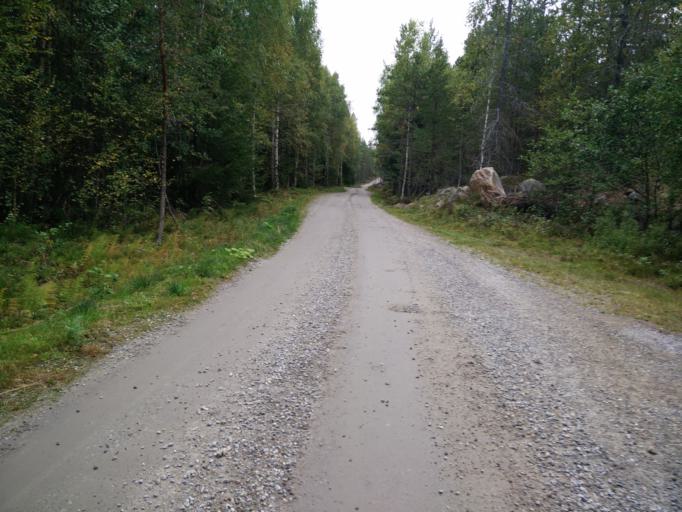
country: SE
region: Gaevleborg
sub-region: Hudiksvalls Kommun
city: Hudiksvall
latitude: 61.8336
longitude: 17.3287
